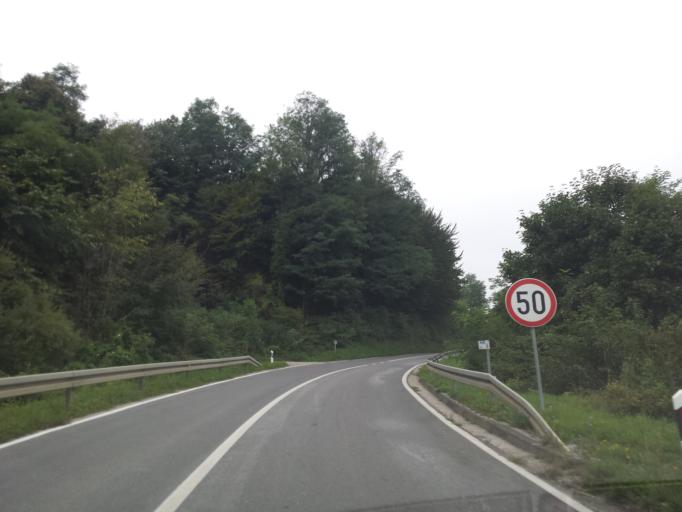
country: HR
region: Karlovacka
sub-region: Grad Karlovac
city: Karlovac
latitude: 45.4198
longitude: 15.4643
